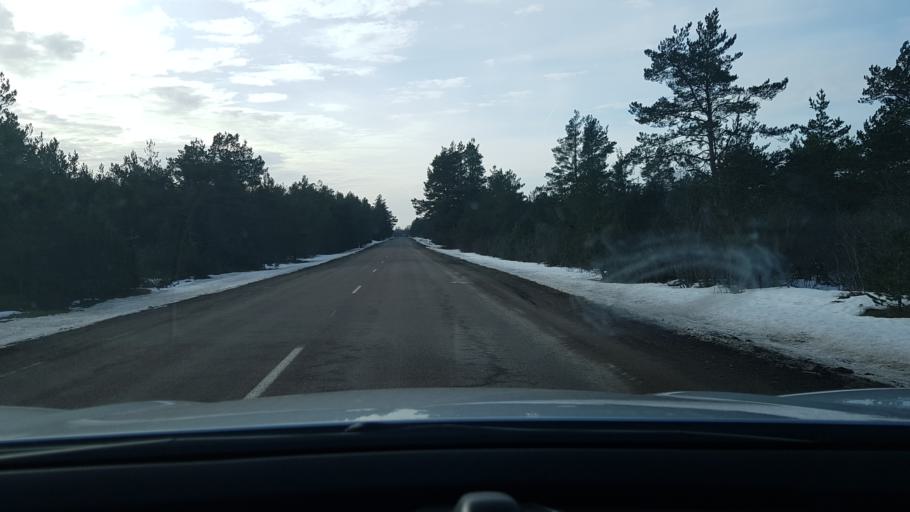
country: EE
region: Saare
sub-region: Kuressaare linn
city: Kuressaare
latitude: 58.3243
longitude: 22.5533
